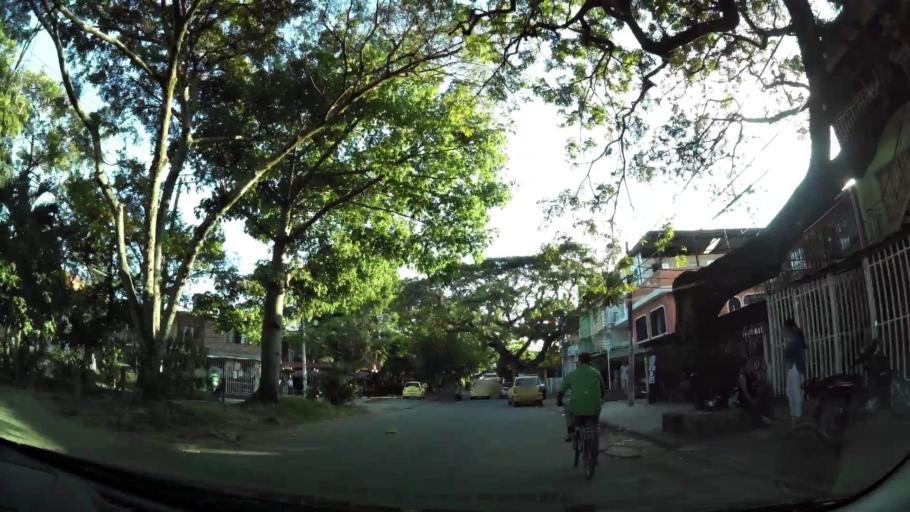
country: CO
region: Valle del Cauca
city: Cali
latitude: 3.4294
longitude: -76.5111
